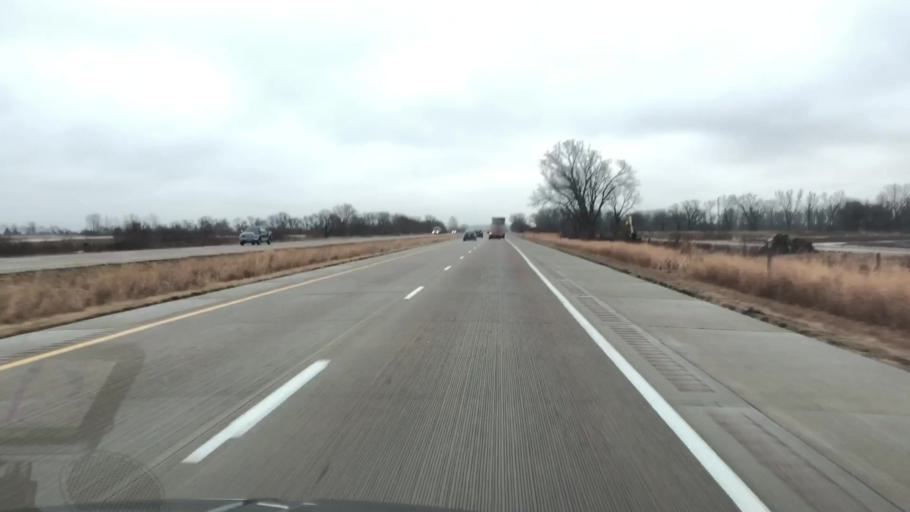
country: US
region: Nebraska
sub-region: Burt County
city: Tekamah
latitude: 41.8464
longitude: -96.0951
